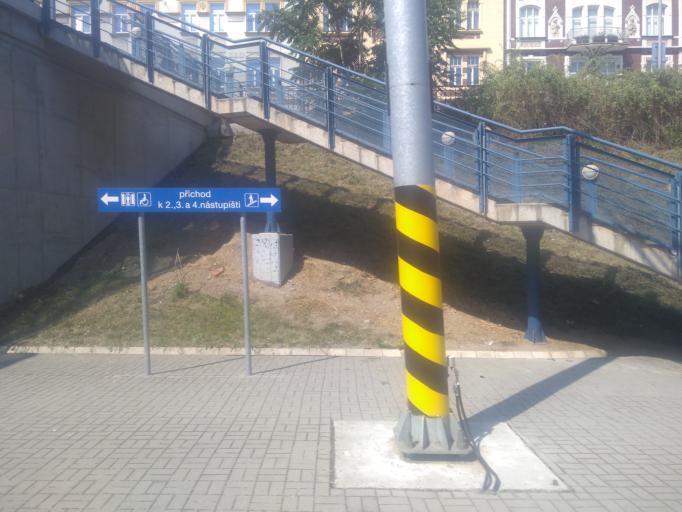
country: CZ
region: Plzensky
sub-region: Okres Plzen-Mesto
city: Pilsen
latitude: 49.7406
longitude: 13.3673
